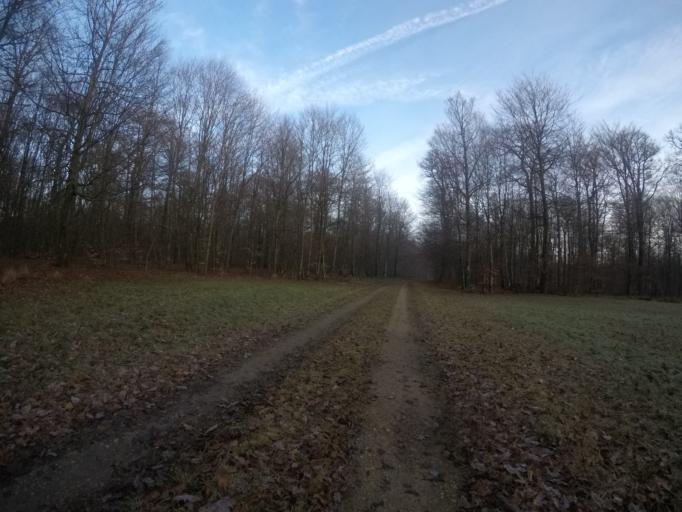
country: BE
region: Wallonia
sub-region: Province du Luxembourg
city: Habay-la-Vieille
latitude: 49.7565
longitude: 5.6691
